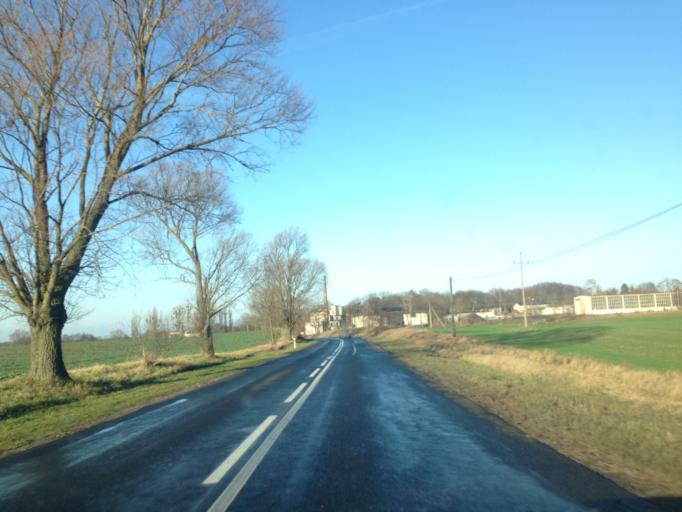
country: PL
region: Kujawsko-Pomorskie
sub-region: Powiat brodnicki
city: Bobrowo
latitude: 53.3405
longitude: 19.2189
